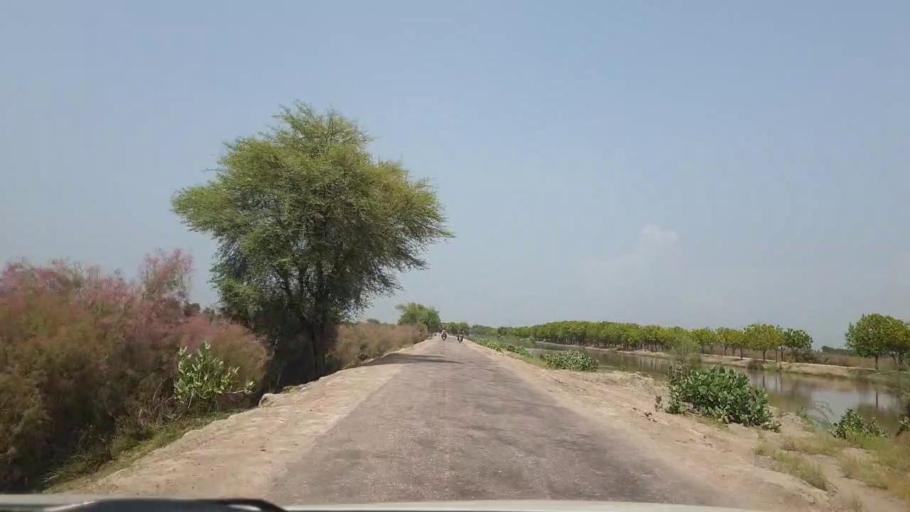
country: PK
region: Sindh
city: Dokri
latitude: 27.3513
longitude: 68.1124
